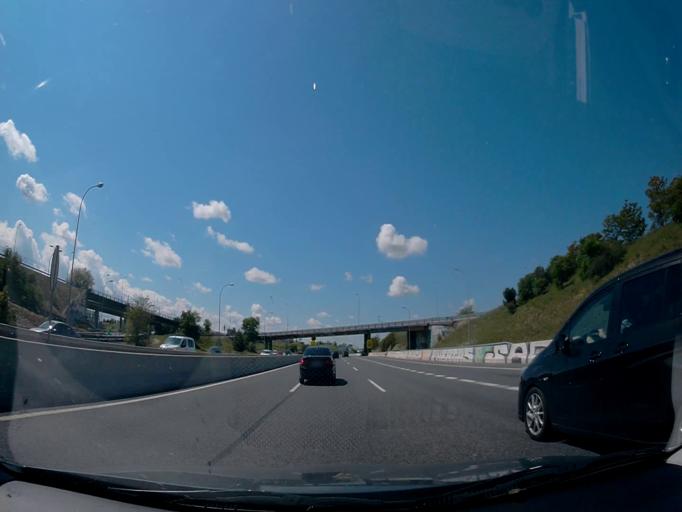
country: ES
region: Madrid
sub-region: Provincia de Madrid
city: Puente de Vallecas
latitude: 40.3739
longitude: -3.6540
